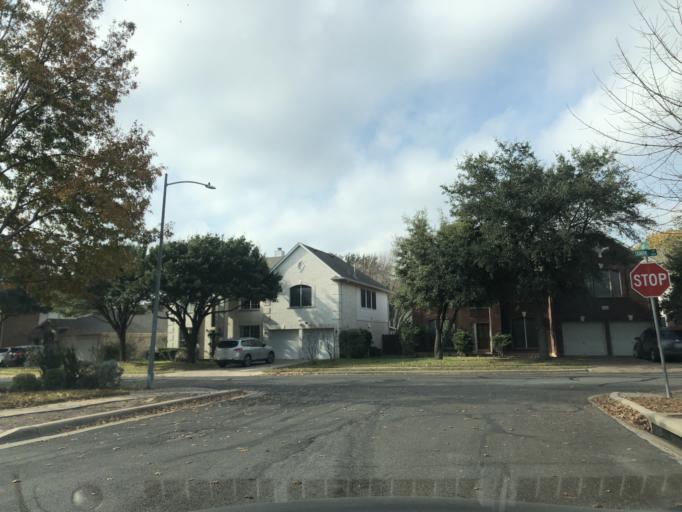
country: US
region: Texas
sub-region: Travis County
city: Wells Branch
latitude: 30.4191
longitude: -97.6792
